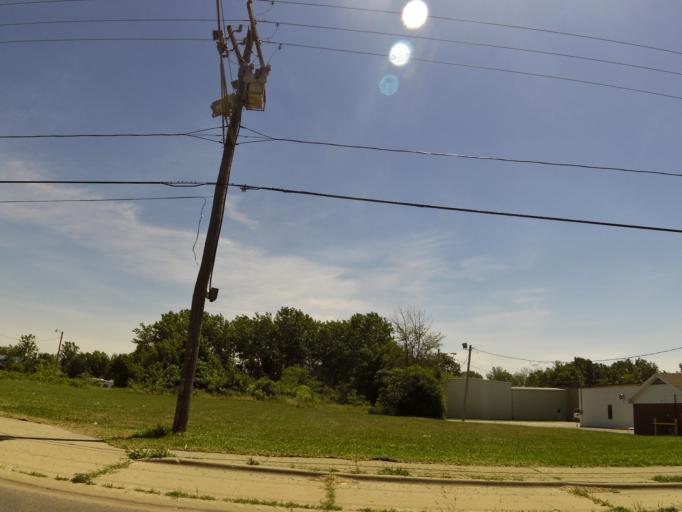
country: US
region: Illinois
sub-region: Vermilion County
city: Danville
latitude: 40.1914
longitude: -87.6294
